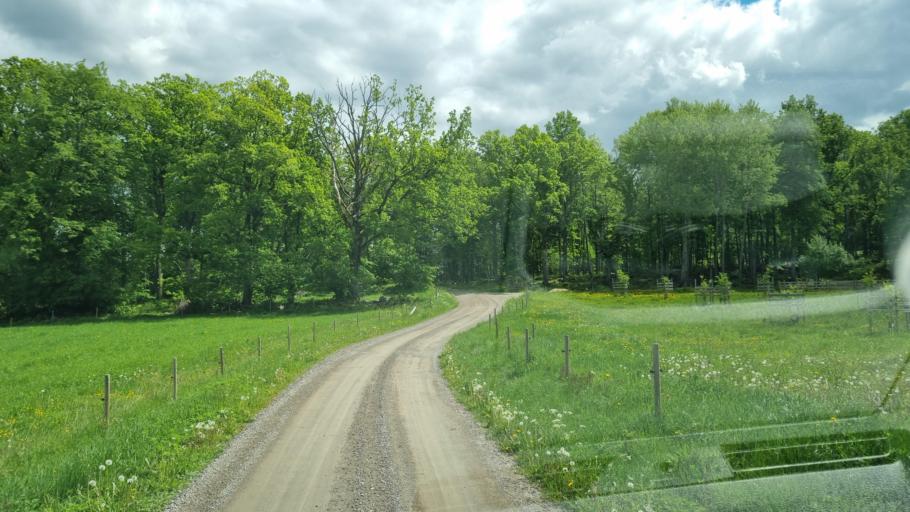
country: SE
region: OEstergoetland
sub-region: Atvidabergs Kommun
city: Atvidaberg
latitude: 58.1920
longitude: 16.0354
